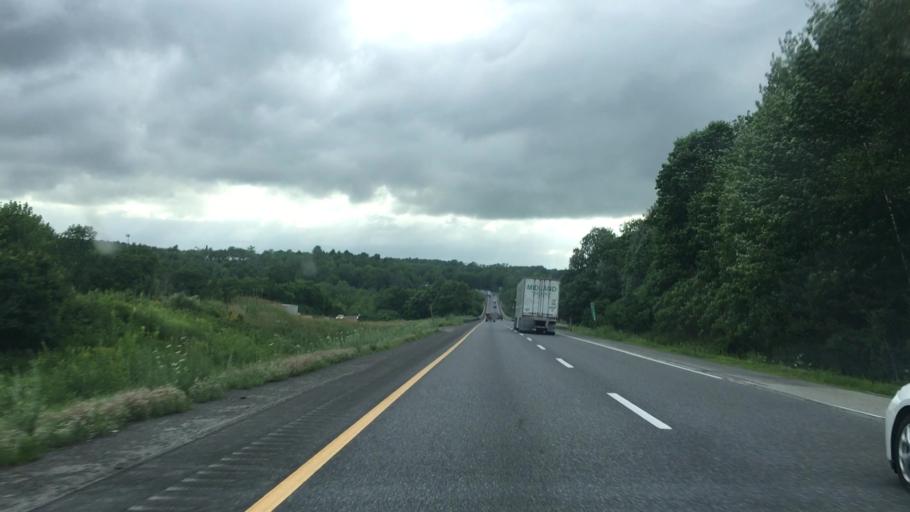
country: US
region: Maine
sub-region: Kennebec County
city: Waterville
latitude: 44.5718
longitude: -69.6468
